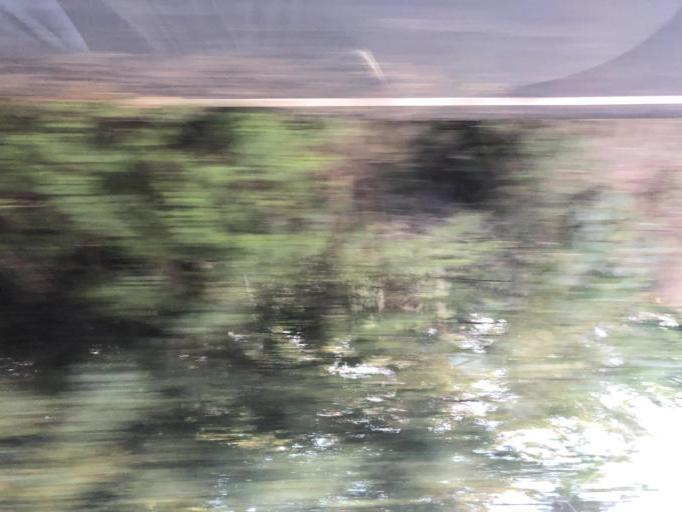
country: TW
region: Taiwan
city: Xinying
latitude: 23.1557
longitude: 120.2761
